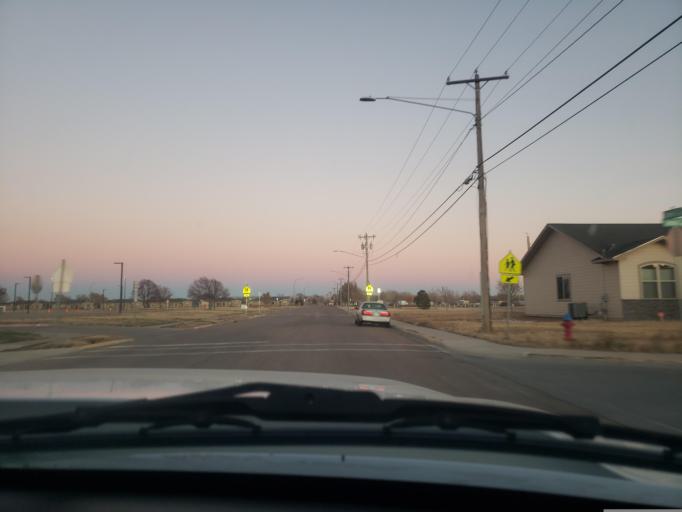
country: US
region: Kansas
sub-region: Finney County
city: Garden City
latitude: 37.9676
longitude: -100.8331
